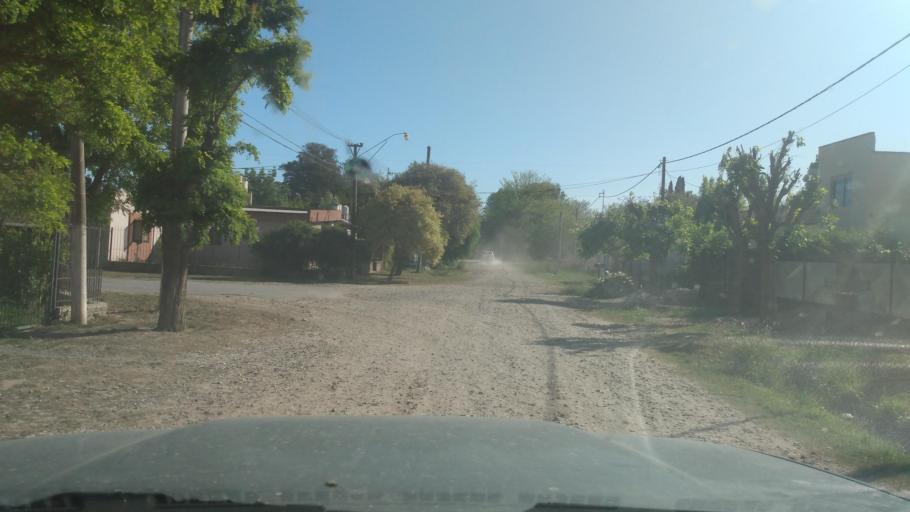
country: AR
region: Buenos Aires
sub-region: Partido de Lujan
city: Lujan
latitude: -34.5618
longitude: -59.1423
